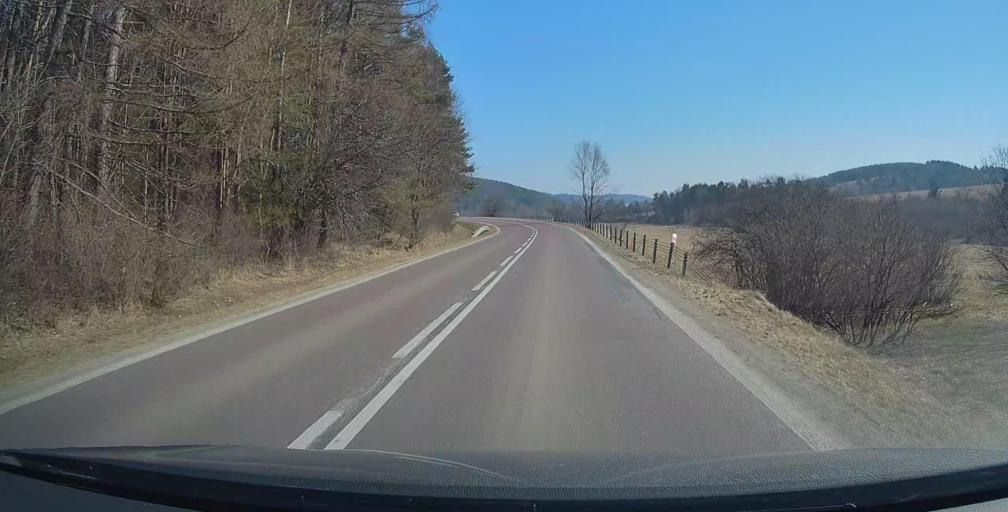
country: PL
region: Subcarpathian Voivodeship
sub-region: Powiat przemyski
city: Bircza
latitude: 49.5916
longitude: 22.5219
